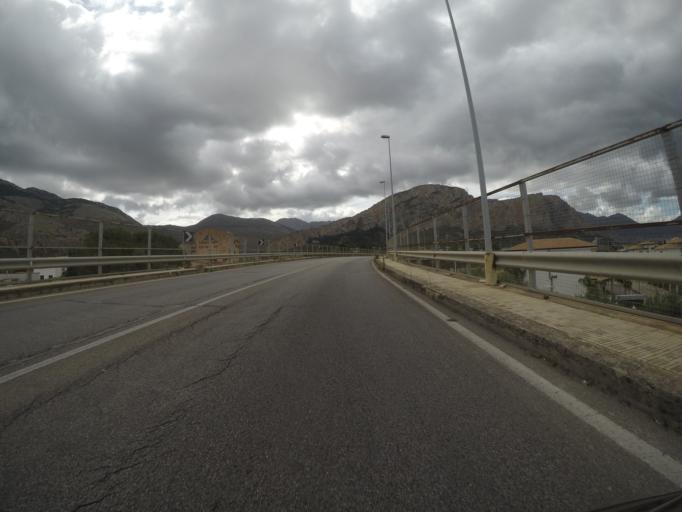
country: IT
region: Sicily
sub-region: Palermo
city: Capaci
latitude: 38.1681
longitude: 13.2219
